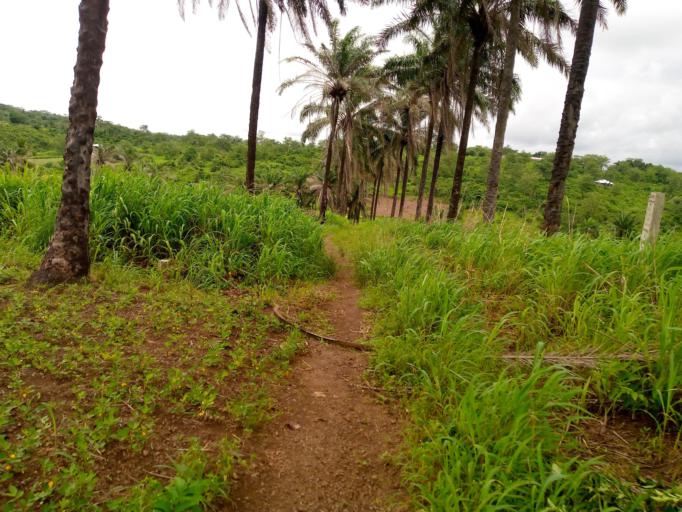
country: SL
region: Southern Province
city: Moyamba
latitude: 8.1531
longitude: -12.4439
